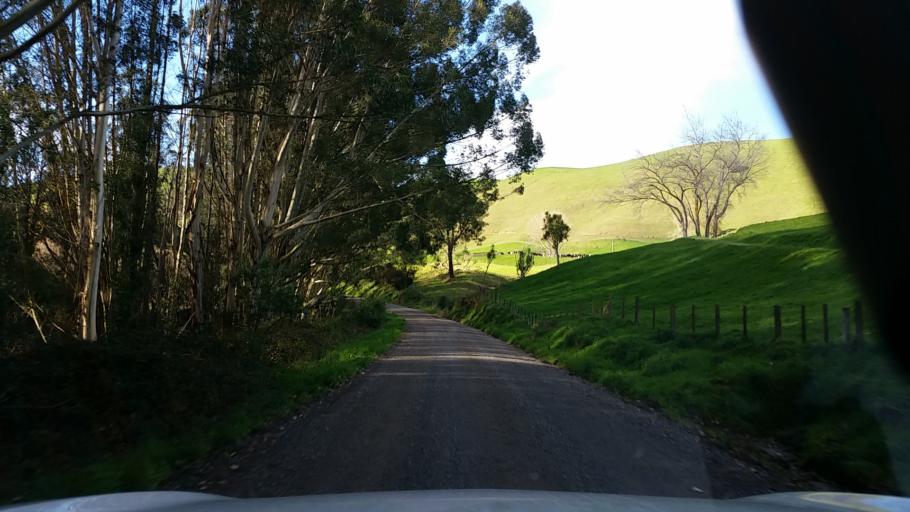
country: NZ
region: Bay of Plenty
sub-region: Rotorua District
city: Rotorua
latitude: -38.3597
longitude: 176.2172
